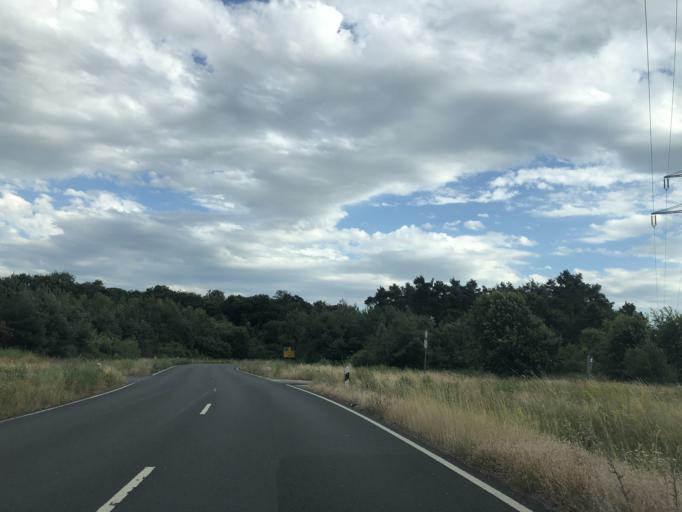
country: DE
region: Hesse
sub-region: Regierungsbezirk Darmstadt
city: Dietzenbach
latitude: 50.0153
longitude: 8.8051
